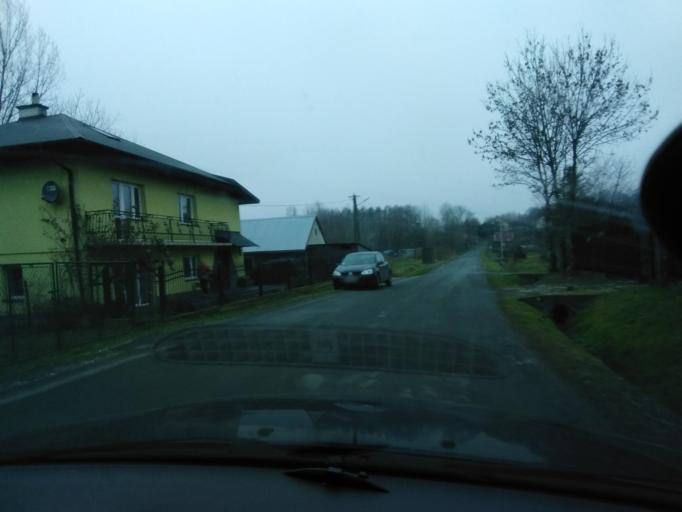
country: PL
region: Subcarpathian Voivodeship
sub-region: Powiat przeworski
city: Zarzecze
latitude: 49.9650
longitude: 22.5665
